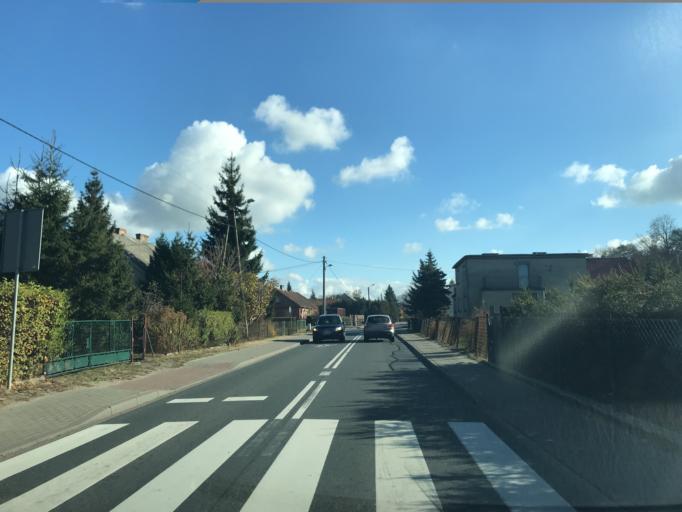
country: PL
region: Warmian-Masurian Voivodeship
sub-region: Powiat ostrodzki
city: Milomlyn
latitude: 53.6654
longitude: 19.8195
